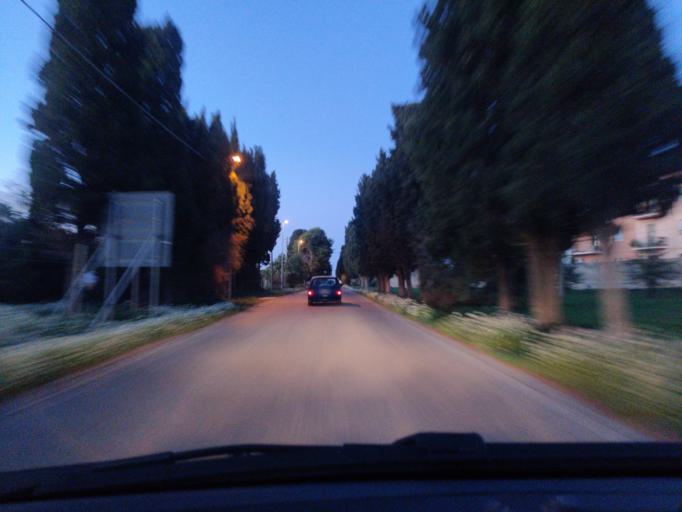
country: IT
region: Latium
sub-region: Citta metropolitana di Roma Capitale
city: Aurelia
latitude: 42.1343
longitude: 11.7882
